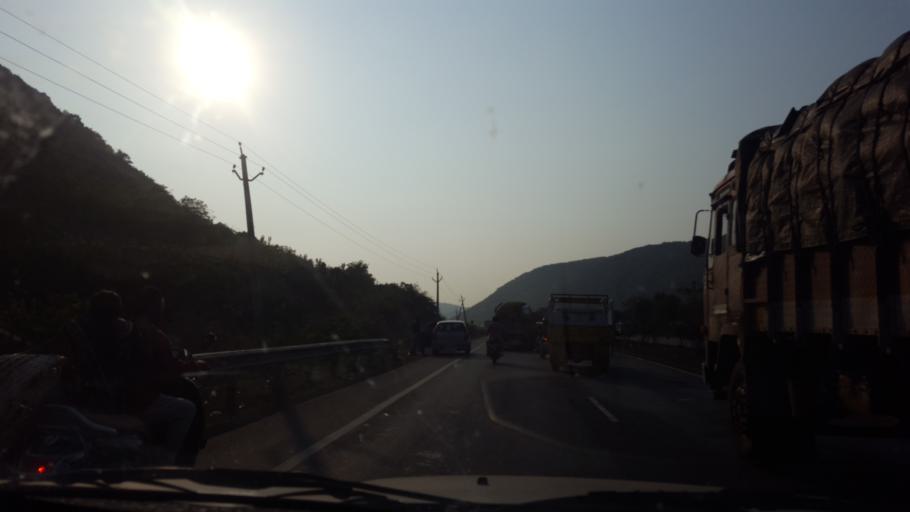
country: IN
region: Andhra Pradesh
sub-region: East Godavari
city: Tuni
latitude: 17.3012
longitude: 82.4328
